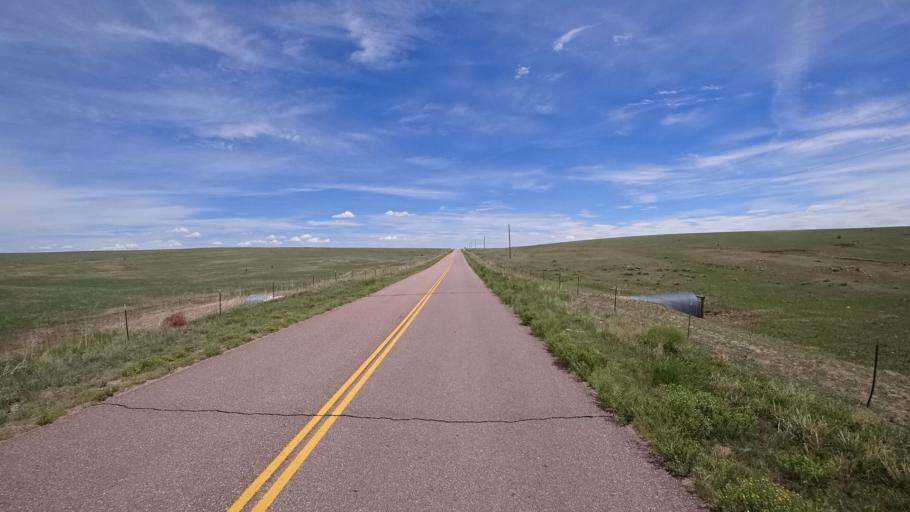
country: US
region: Colorado
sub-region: El Paso County
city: Fountain
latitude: 38.6941
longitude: -104.6161
